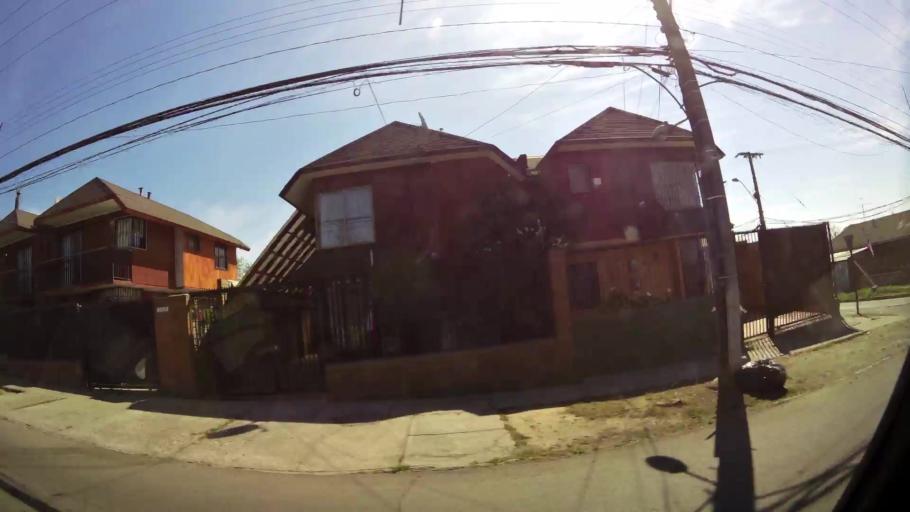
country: CL
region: Santiago Metropolitan
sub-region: Provincia de Santiago
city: Lo Prado
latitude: -33.5025
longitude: -70.7175
